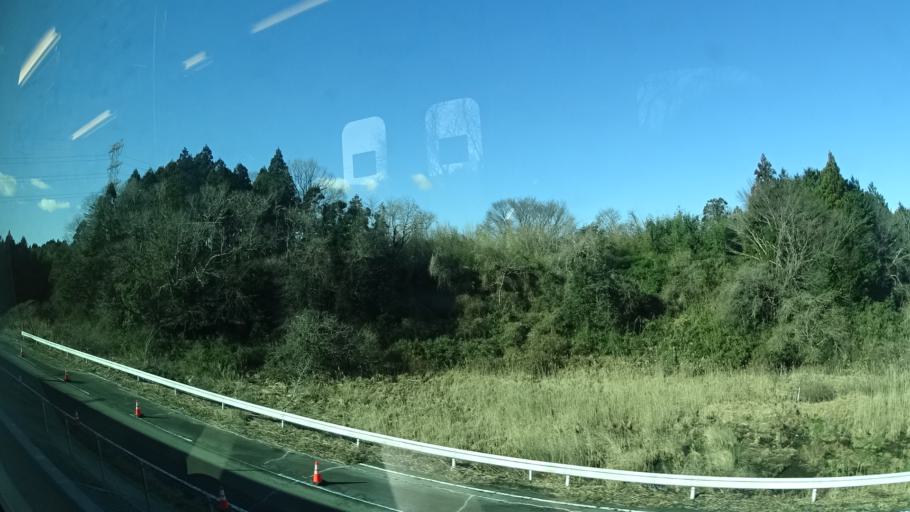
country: JP
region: Fukushima
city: Namie
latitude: 37.4298
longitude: 141.0012
